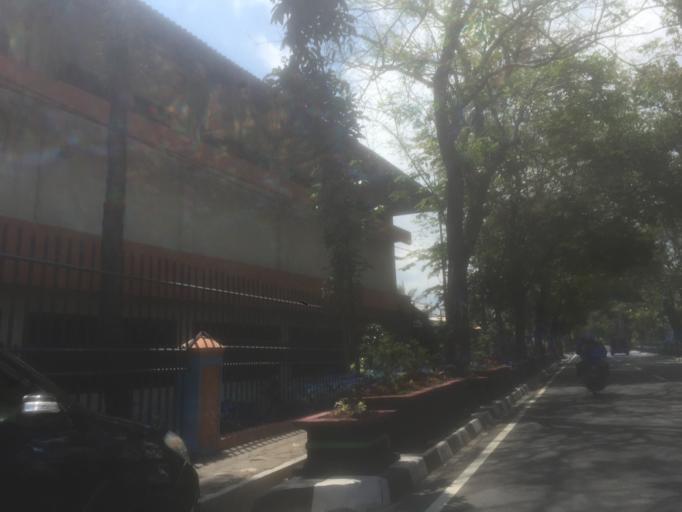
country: ID
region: Central Java
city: Muntilan
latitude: -7.5757
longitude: 110.2698
